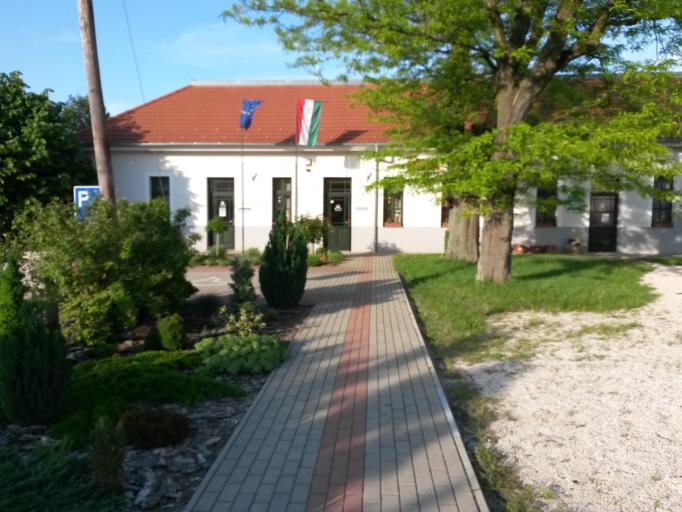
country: HU
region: Veszprem
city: Zanka
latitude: 46.9137
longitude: 17.6752
